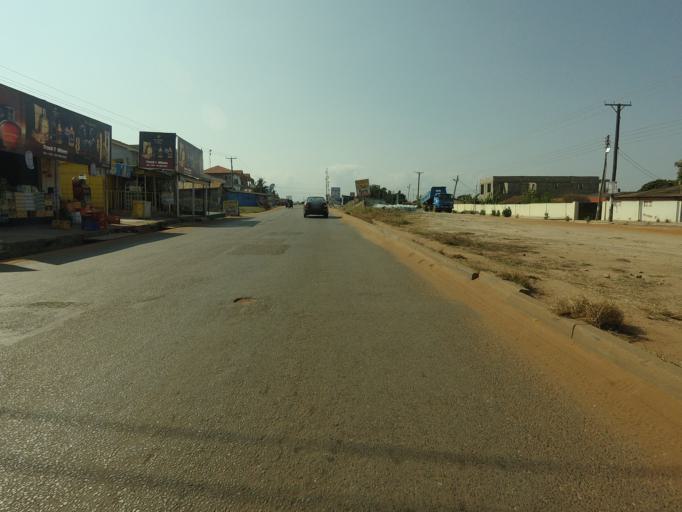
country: GH
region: Greater Accra
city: Teshi Old Town
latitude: 5.6075
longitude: -0.1064
